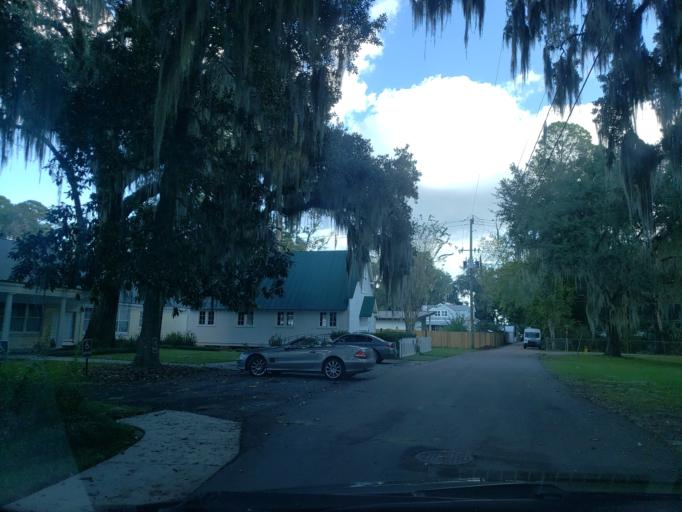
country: US
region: Georgia
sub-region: Chatham County
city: Isle of Hope
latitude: 31.9833
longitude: -81.0575
